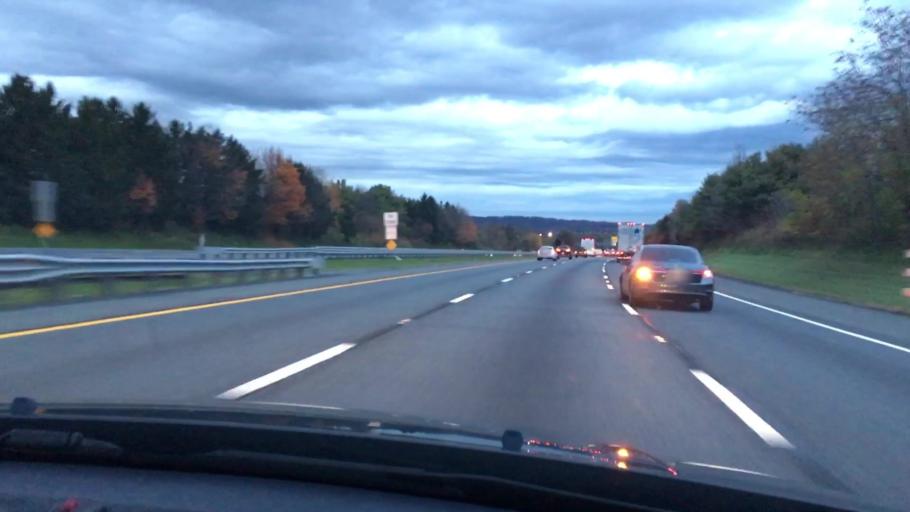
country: US
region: New Jersey
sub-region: Warren County
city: Alpha
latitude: 40.6584
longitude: -75.1722
